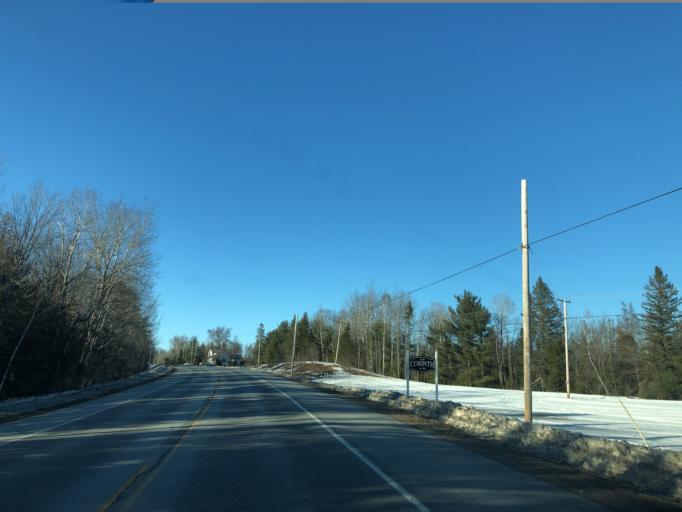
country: US
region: Maine
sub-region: Penobscot County
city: Kenduskeag
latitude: 44.9455
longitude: -68.9453
